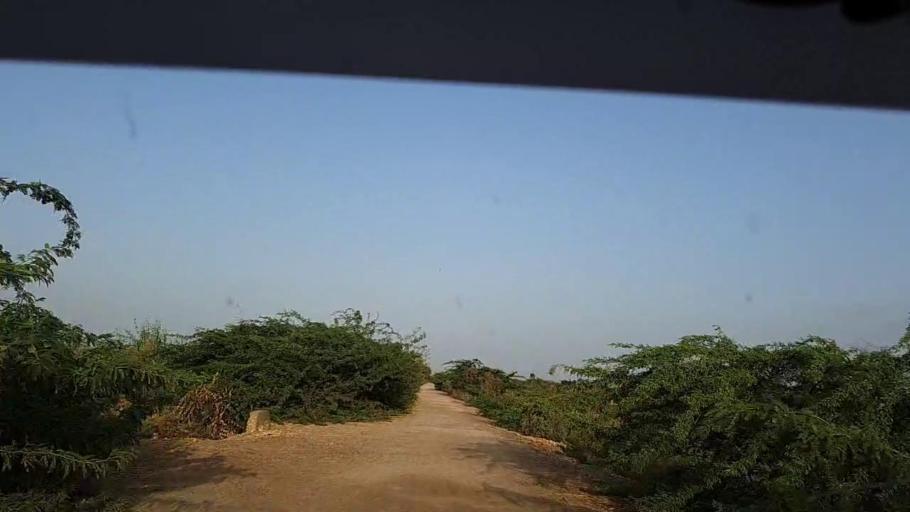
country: PK
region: Sindh
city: Kadhan
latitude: 24.5468
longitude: 68.9493
